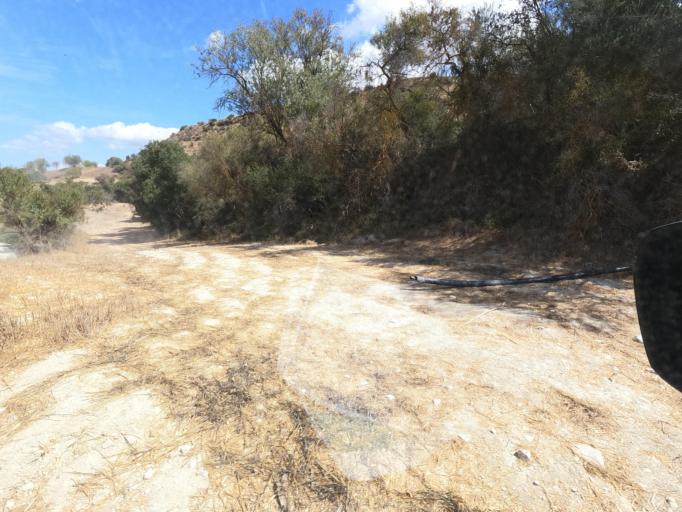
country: CY
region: Pafos
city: Mesogi
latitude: 34.8319
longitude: 32.5451
